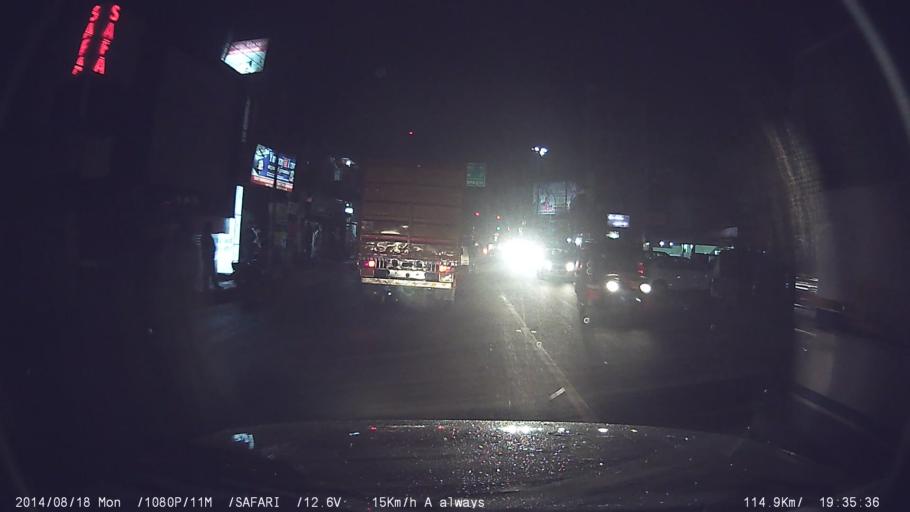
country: IN
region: Kerala
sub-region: Ernakulam
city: Perumpavur
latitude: 10.1136
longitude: 76.4784
